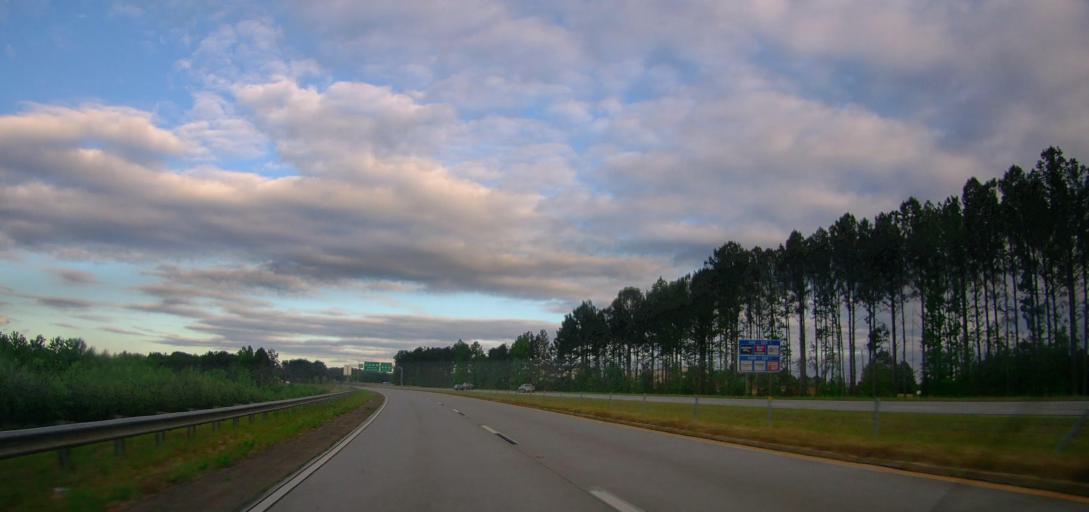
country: US
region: Georgia
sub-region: Oconee County
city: Watkinsville
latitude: 33.9157
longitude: -83.4585
